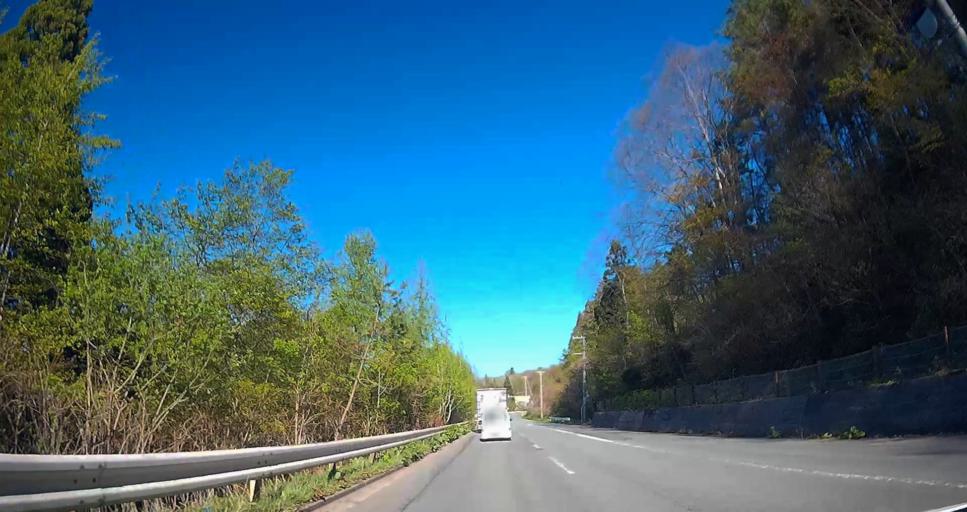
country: JP
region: Aomori
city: Mutsu
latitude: 41.4332
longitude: 141.1332
